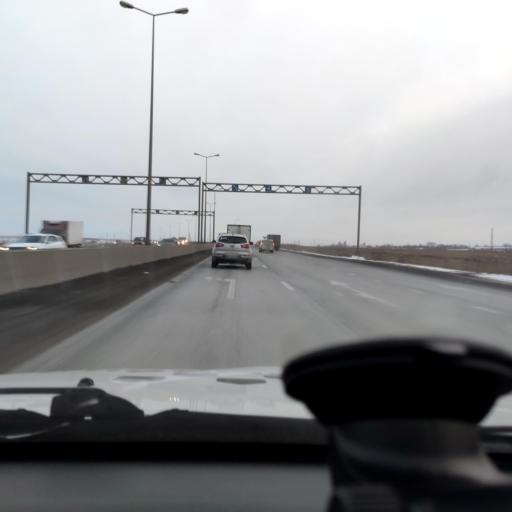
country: RU
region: Perm
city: Kondratovo
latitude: 57.9330
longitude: 56.1638
